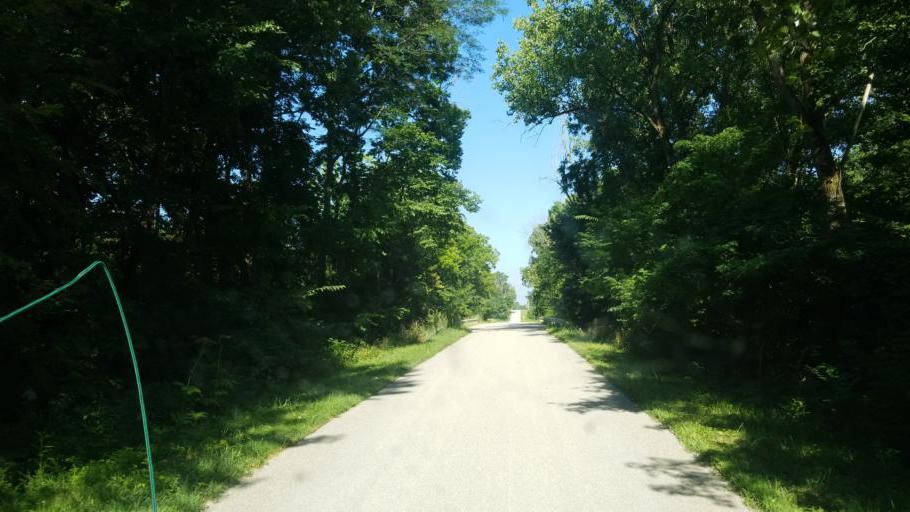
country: US
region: Ohio
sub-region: Wyandot County
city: Upper Sandusky
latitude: 40.7883
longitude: -83.3581
